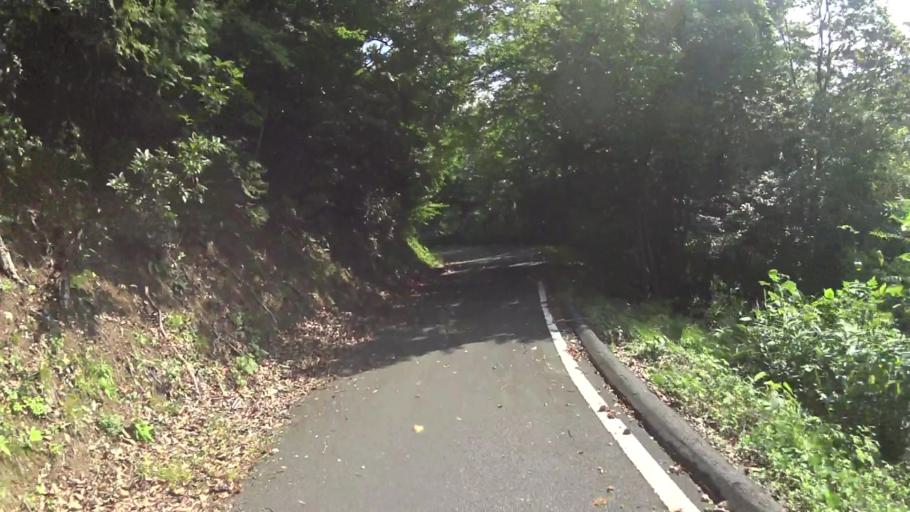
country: JP
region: Kyoto
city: Miyazu
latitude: 35.6569
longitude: 135.2409
